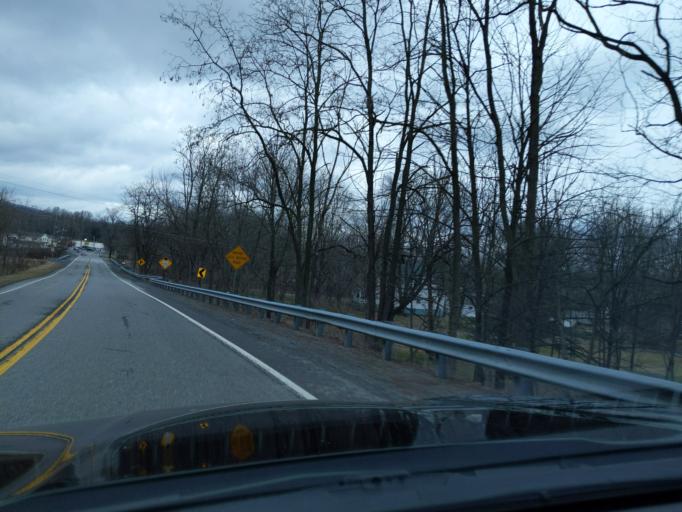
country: US
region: Pennsylvania
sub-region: Blair County
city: Bellwood
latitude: 40.5921
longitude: -78.3361
